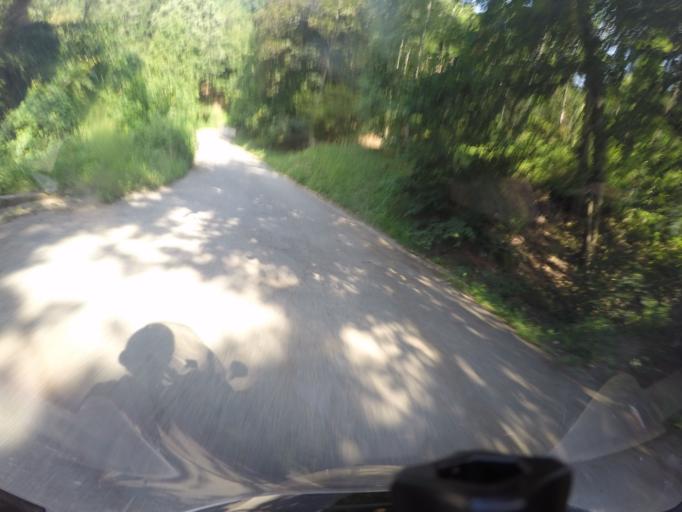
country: IT
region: Lombardy
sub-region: Provincia di Lecco
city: Santa Maria Hoe
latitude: 45.7543
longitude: 9.3924
